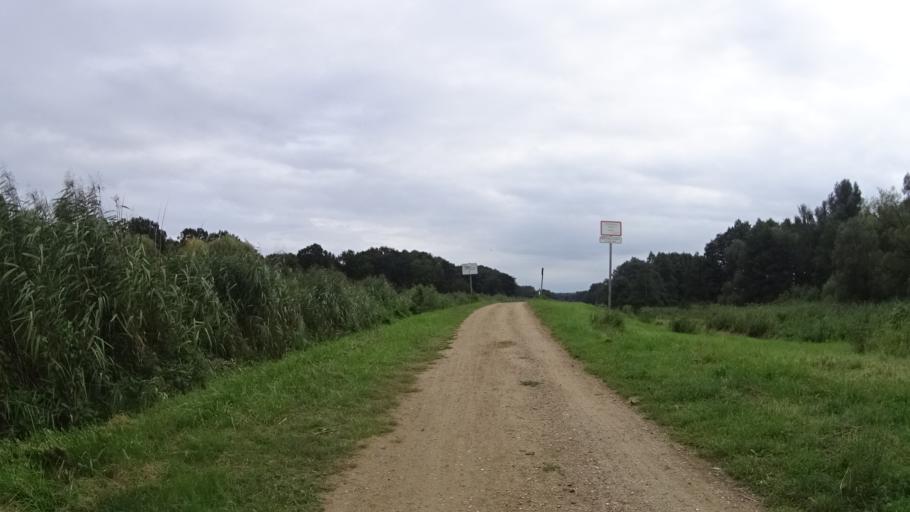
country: DE
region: Schleswig-Holstein
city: Panten
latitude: 53.6699
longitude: 10.6366
